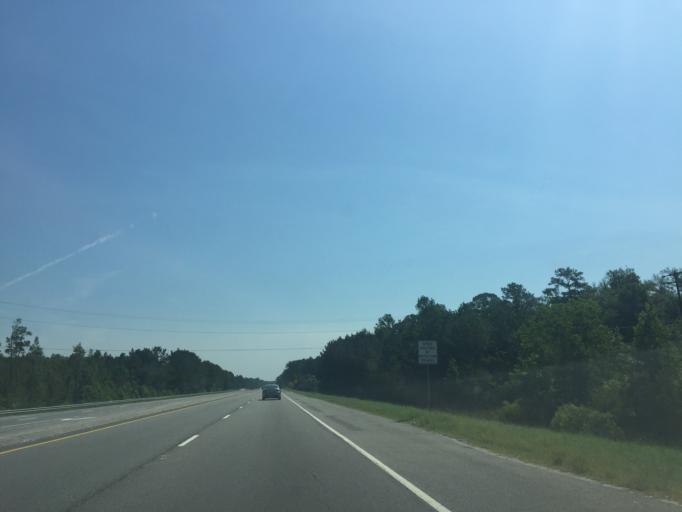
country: US
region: Georgia
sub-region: Bryan County
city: Richmond Hill
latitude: 31.9807
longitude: -81.2867
